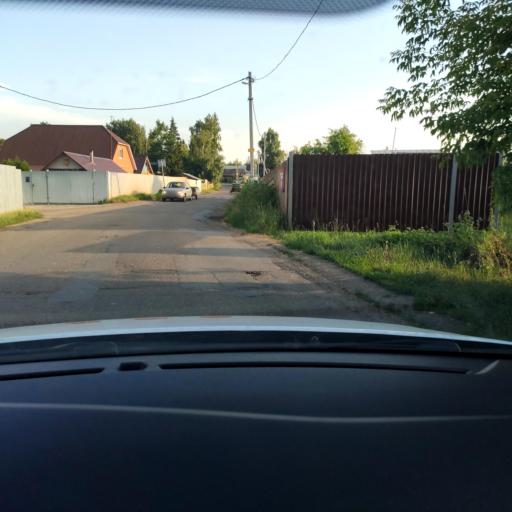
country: RU
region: Tatarstan
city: Vysokaya Gora
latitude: 55.9774
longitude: 49.3068
